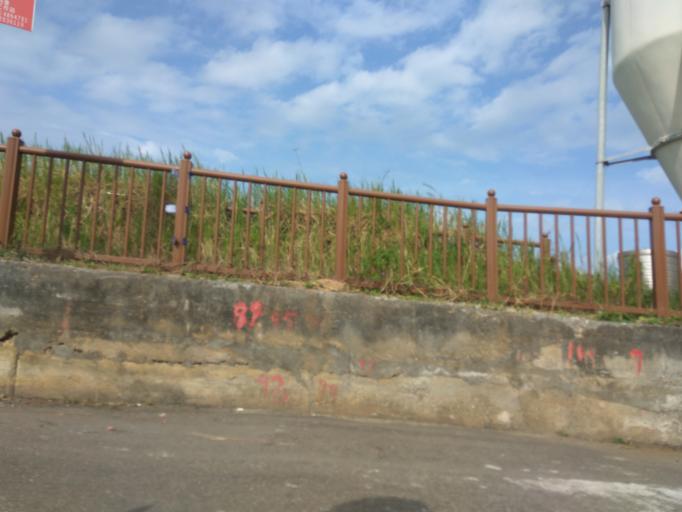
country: TW
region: Taiwan
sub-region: Hsinchu
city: Zhubei
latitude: 24.9764
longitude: 121.0267
